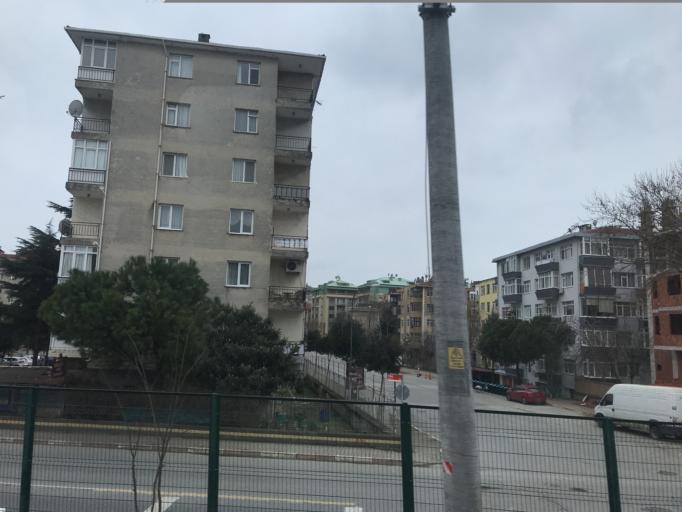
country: TR
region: Istanbul
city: Maltepe
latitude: 40.9032
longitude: 29.1643
